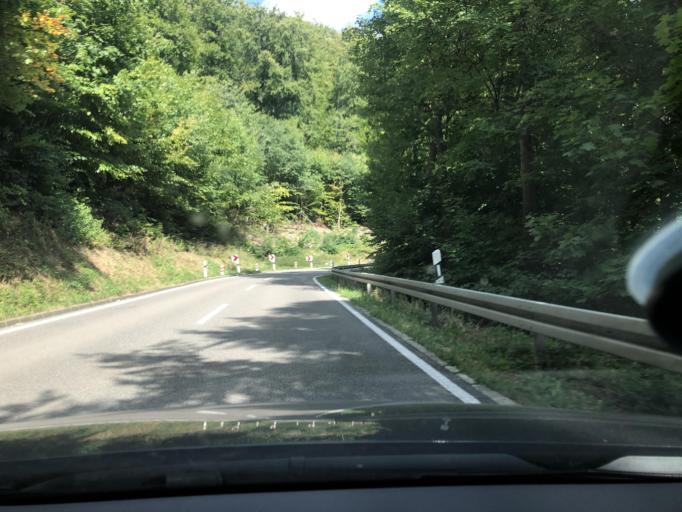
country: DE
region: Baden-Wuerttemberg
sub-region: Tuebingen Region
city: Pfullingen
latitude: 48.4305
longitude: 9.2054
